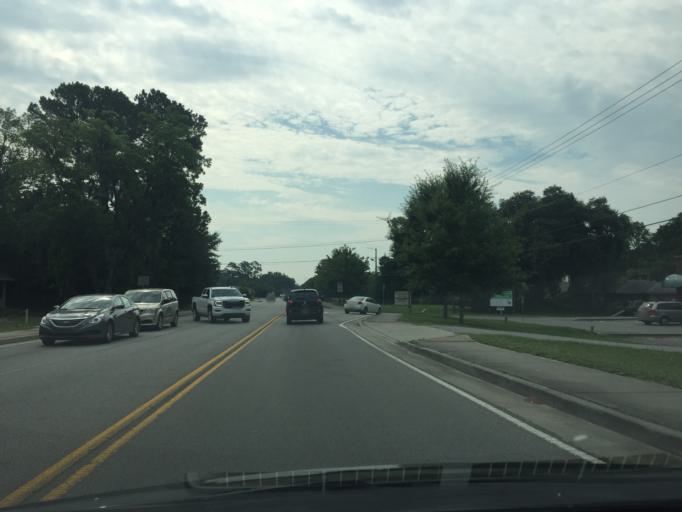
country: US
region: Georgia
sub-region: Chatham County
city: Isle of Hope
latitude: 32.0123
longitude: -81.1078
